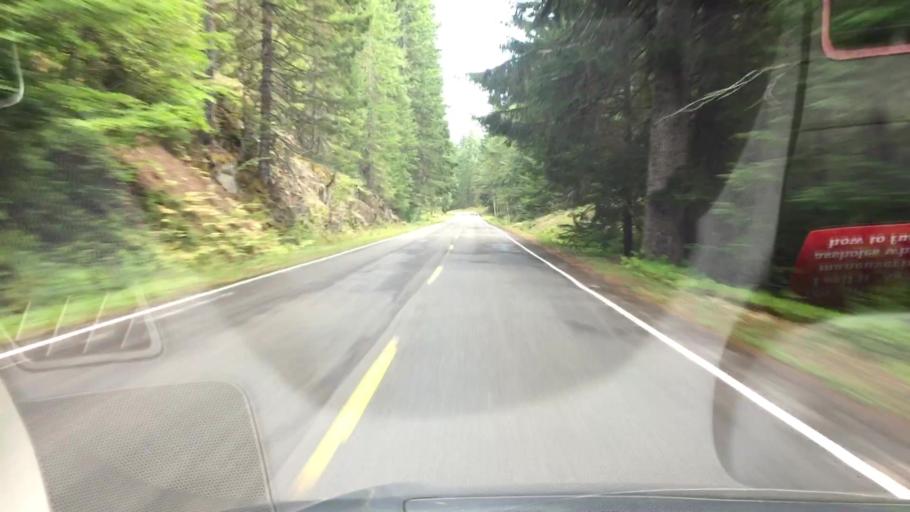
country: US
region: Washington
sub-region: Pierce County
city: Buckley
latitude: 46.7577
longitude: -121.6260
